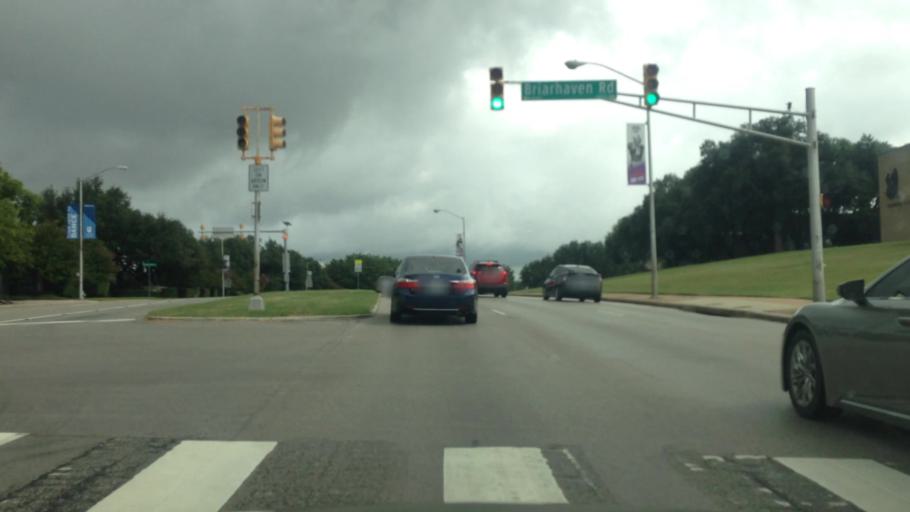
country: US
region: Texas
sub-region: Tarrant County
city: Edgecliff Village
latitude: 32.6889
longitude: -97.3935
